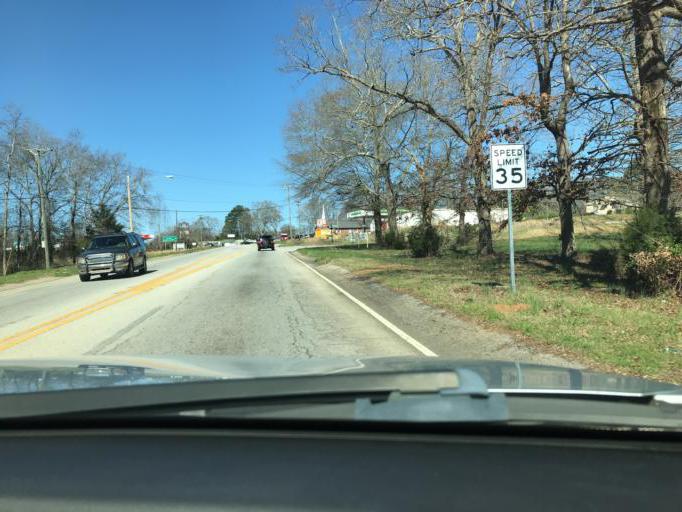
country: US
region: South Carolina
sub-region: Laurens County
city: Watts Mills
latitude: 34.5024
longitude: -81.9926
